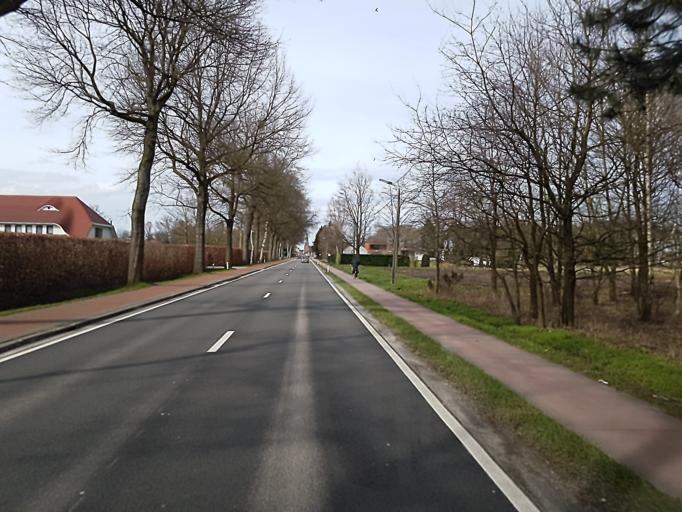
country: BE
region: Flanders
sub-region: Provincie Antwerpen
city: Dessel
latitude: 51.2306
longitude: 5.1142
